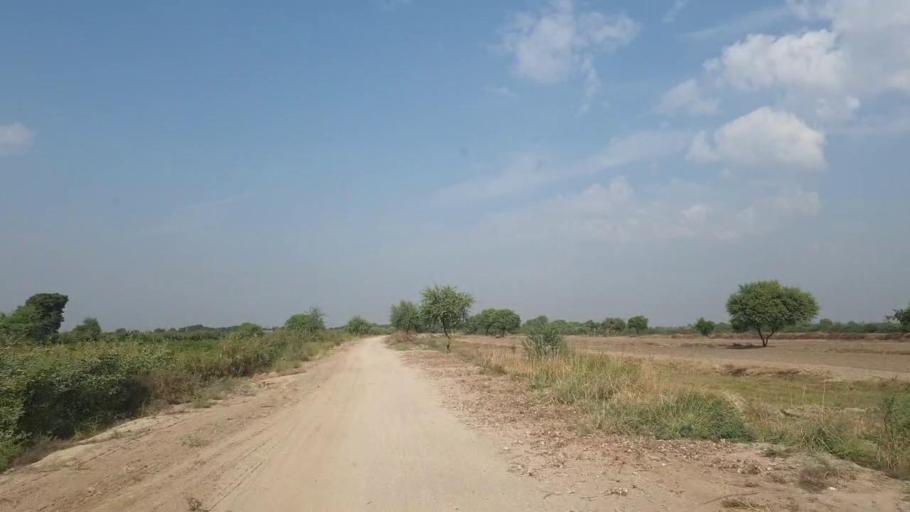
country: PK
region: Sindh
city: Digri
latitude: 25.0147
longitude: 69.0669
